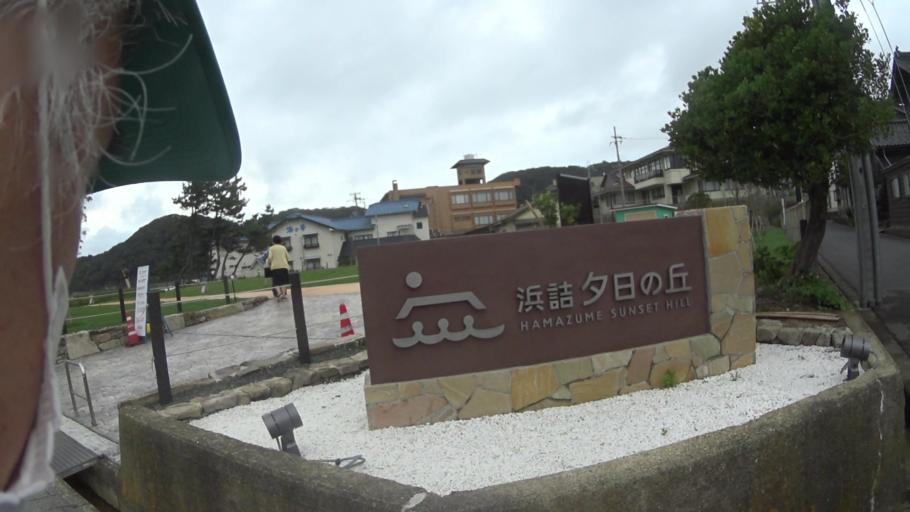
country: JP
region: Hyogo
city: Toyooka
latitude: 35.6633
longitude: 134.9663
